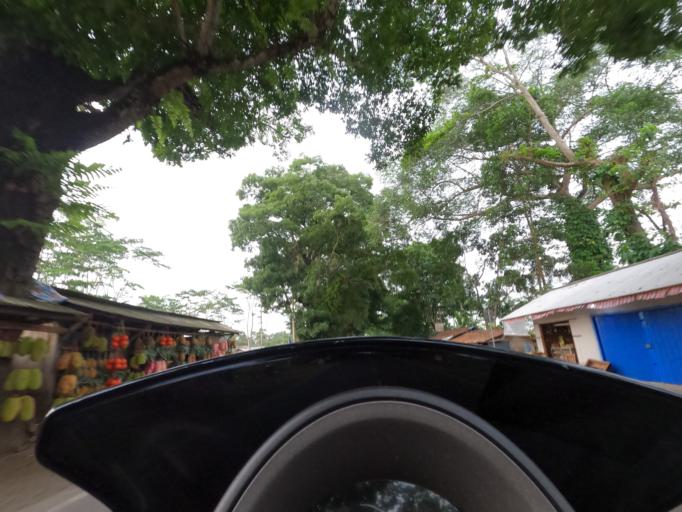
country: ID
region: West Java
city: Lembang
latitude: -6.6723
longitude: 107.6974
